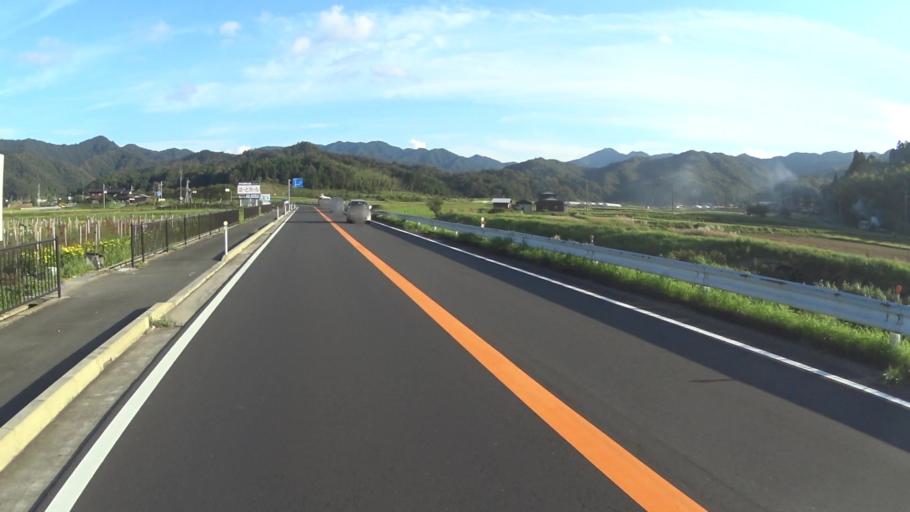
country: JP
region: Hyogo
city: Toyooka
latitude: 35.5763
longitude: 134.9746
